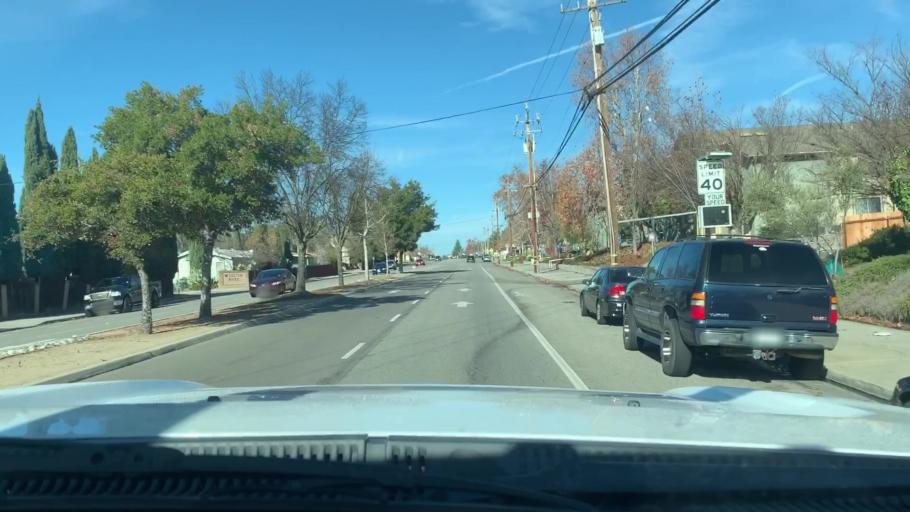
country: US
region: California
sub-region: San Luis Obispo County
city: Atascadero
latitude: 35.4618
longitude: -120.6450
